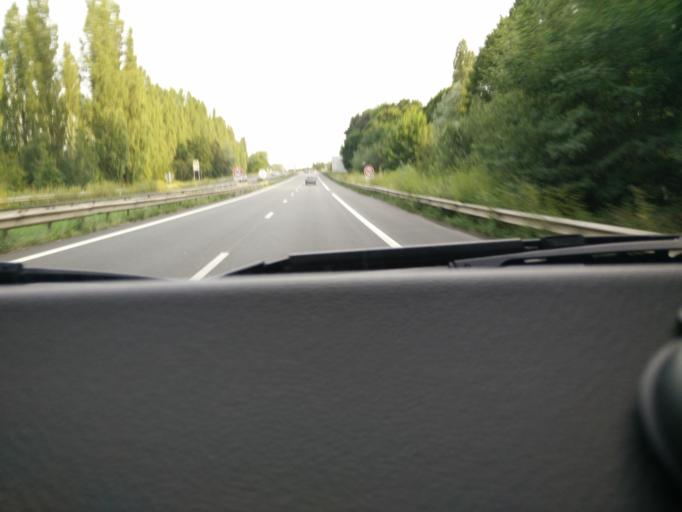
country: FR
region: Nord-Pas-de-Calais
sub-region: Departement du Nord
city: Petite-Foret
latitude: 50.3635
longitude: 3.4846
